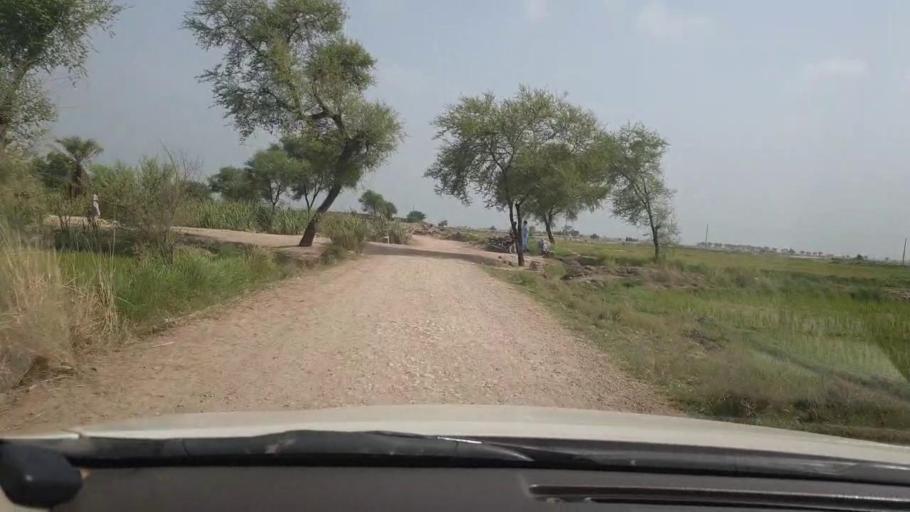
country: PK
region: Sindh
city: Shikarpur
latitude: 28.0144
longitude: 68.5947
